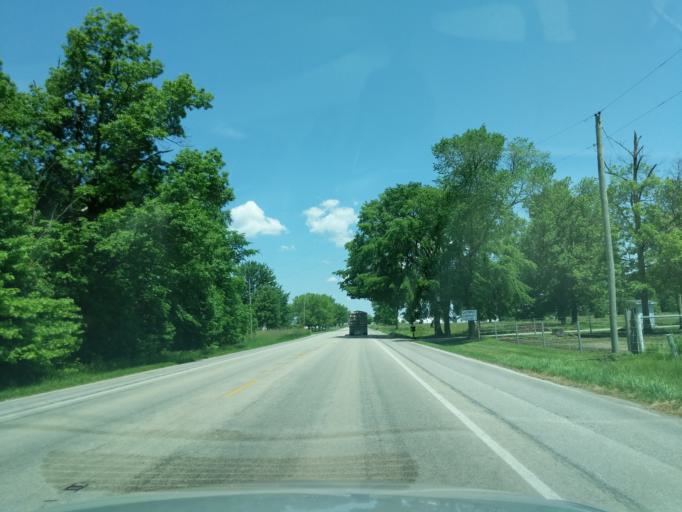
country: US
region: Indiana
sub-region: LaGrange County
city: Topeka
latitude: 41.5692
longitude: -85.5785
